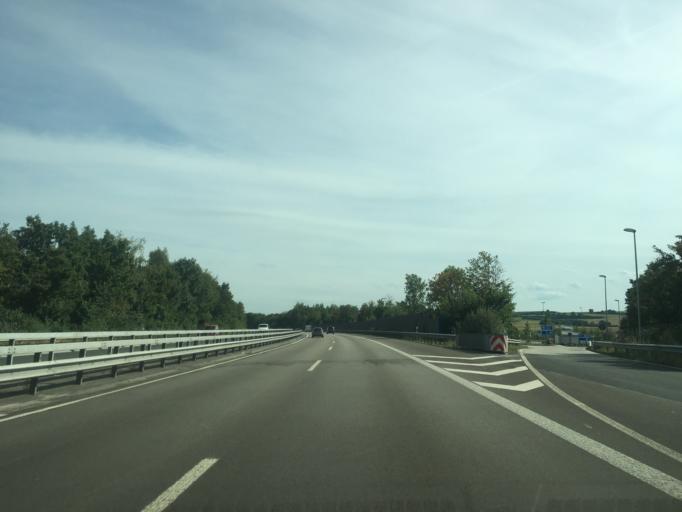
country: DE
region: Rheinland-Pfalz
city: Dintesheim
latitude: 49.7192
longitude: 8.1348
